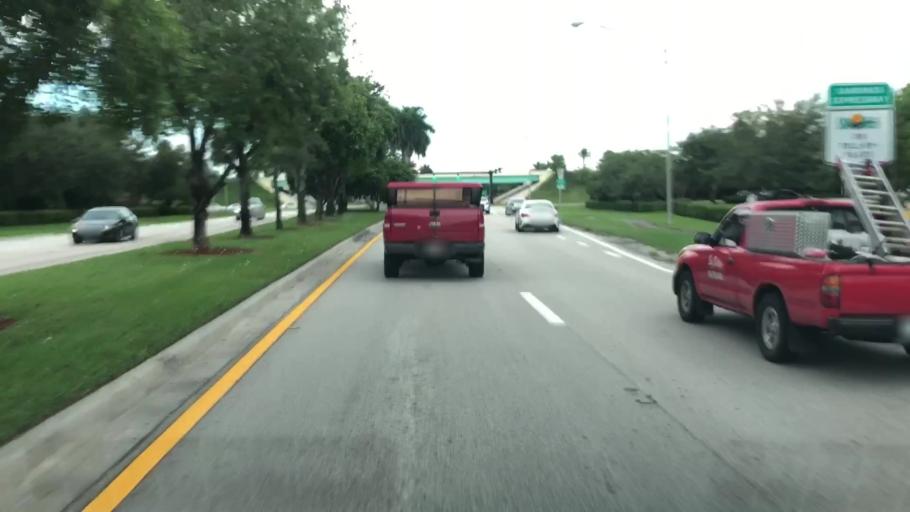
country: US
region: Florida
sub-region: Broward County
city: Coral Springs
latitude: 26.3044
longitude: -80.2788
